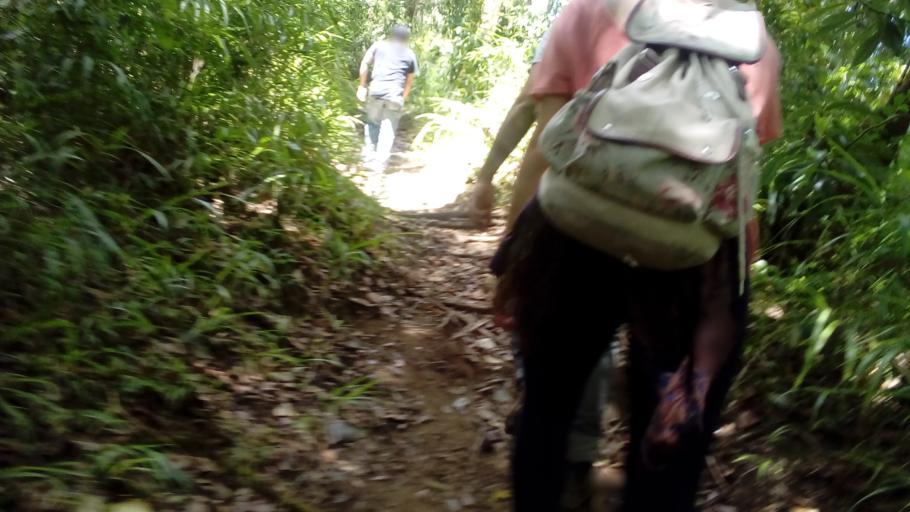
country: CR
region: Alajuela
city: Sabanilla
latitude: 10.1601
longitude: -84.2377
